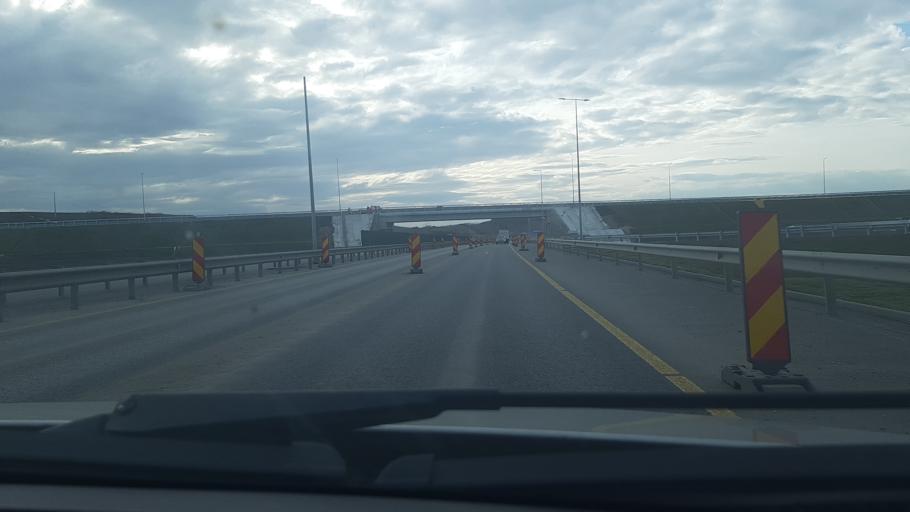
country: RO
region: Mures
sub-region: Comuna Iernut
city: Cipau
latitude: 46.4308
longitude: 24.2702
